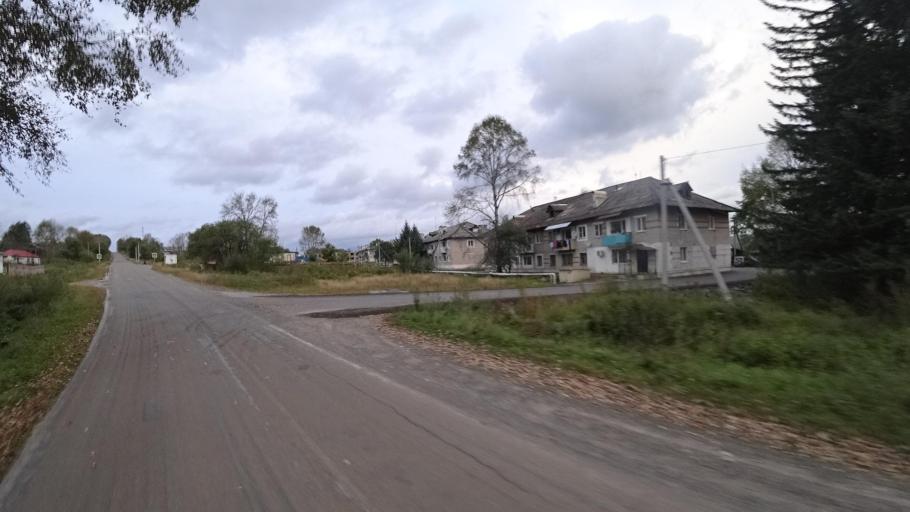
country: RU
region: Jewish Autonomous Oblast
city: Izvestkovyy
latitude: 48.9731
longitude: 131.5804
